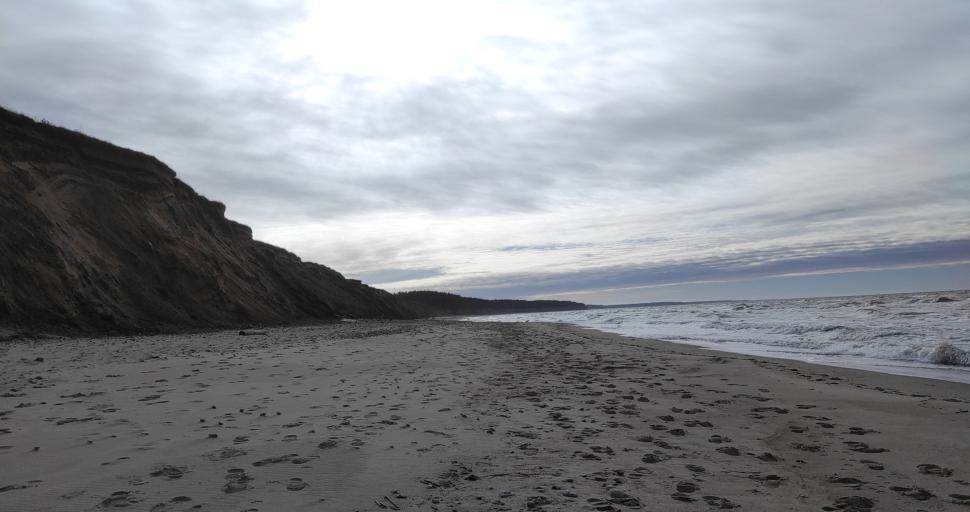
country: LV
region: Alsunga
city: Alsunga
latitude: 57.0406
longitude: 21.4030
